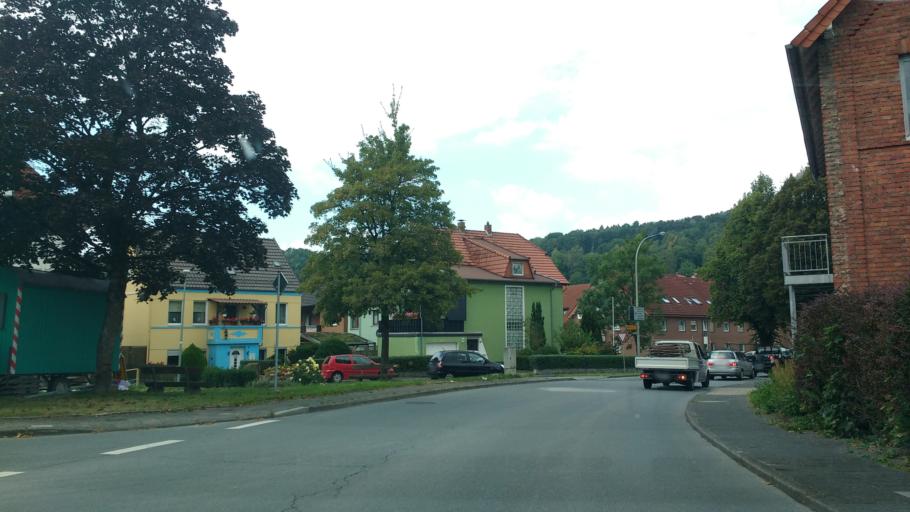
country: DE
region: North Rhine-Westphalia
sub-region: Regierungsbezirk Detmold
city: Altenbeken
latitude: 51.7630
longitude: 8.9356
